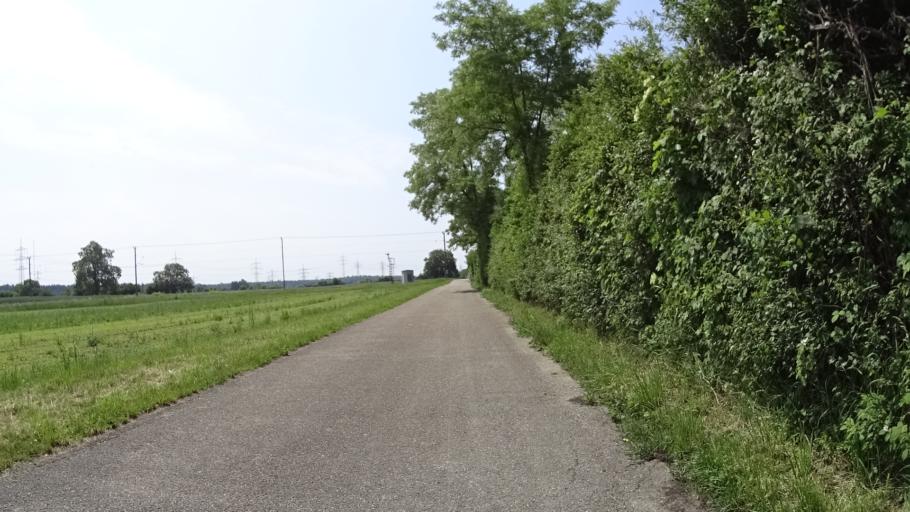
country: DE
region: Baden-Wuerttemberg
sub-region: Karlsruhe Region
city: Eggenstein-Leopoldshafen
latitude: 49.1068
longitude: 8.4110
